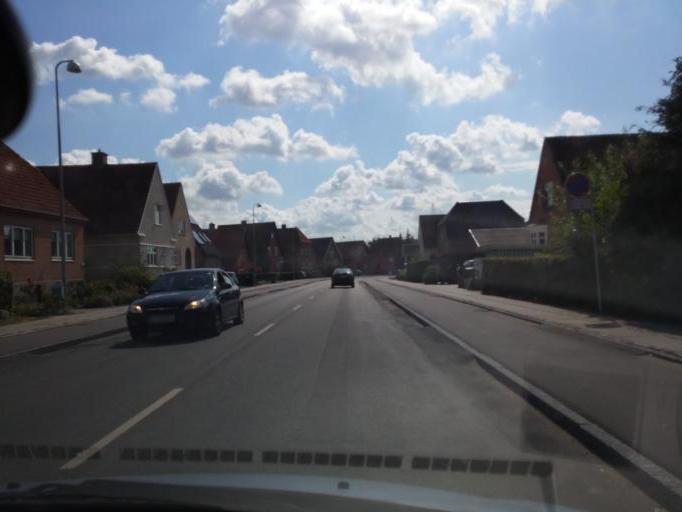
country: DK
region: South Denmark
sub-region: Odense Kommune
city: Odense
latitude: 55.4013
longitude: 10.4124
